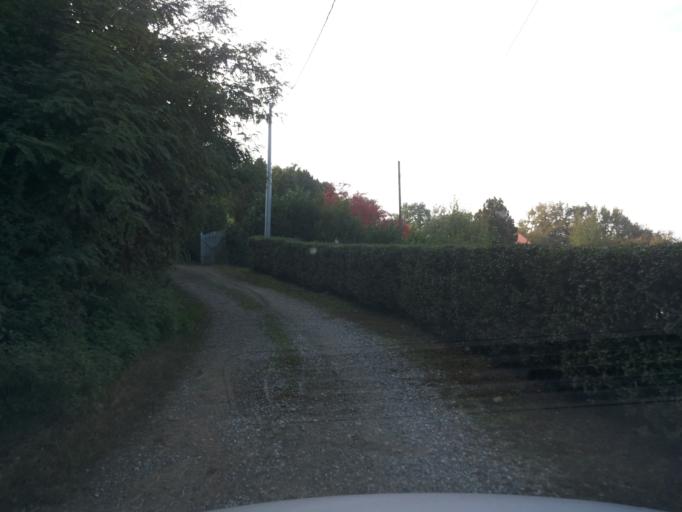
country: IT
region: Piedmont
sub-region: Provincia di Biella
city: Viverone
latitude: 45.4054
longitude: 8.0312
